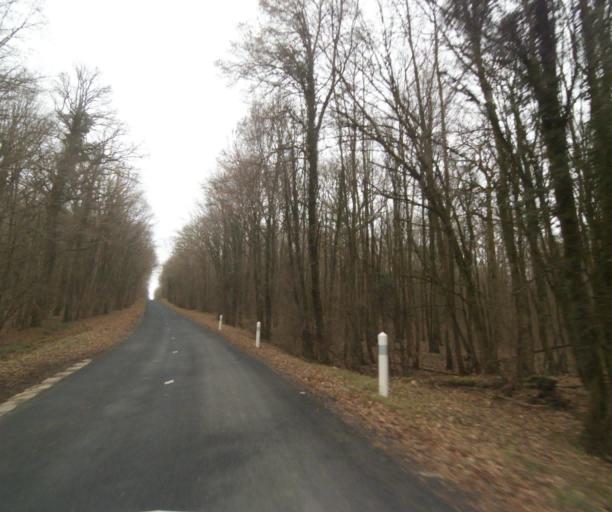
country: FR
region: Champagne-Ardenne
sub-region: Departement de la Haute-Marne
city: Bienville
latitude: 48.5631
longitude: 5.0054
